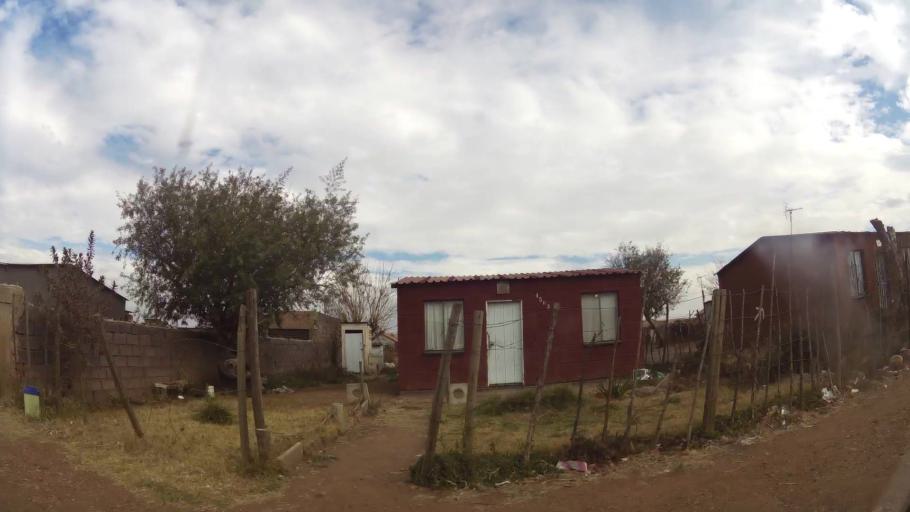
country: ZA
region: Gauteng
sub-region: Ekurhuleni Metropolitan Municipality
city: Germiston
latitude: -26.4067
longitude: 28.1436
